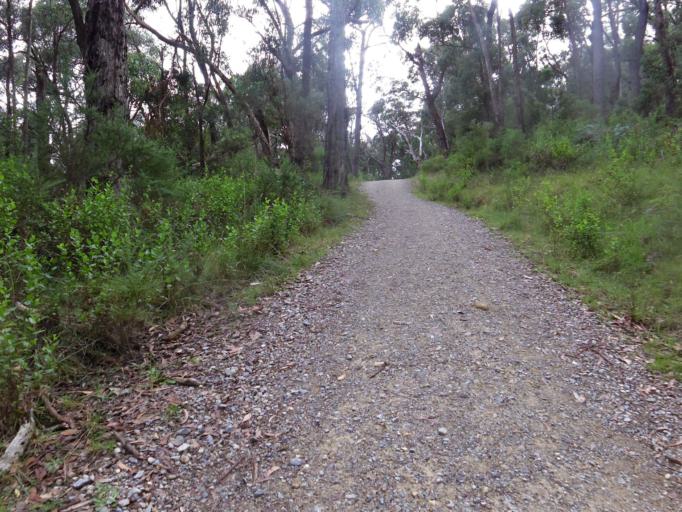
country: AU
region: Victoria
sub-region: Yarra Ranges
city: Montrose
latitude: -37.8376
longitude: 145.3383
